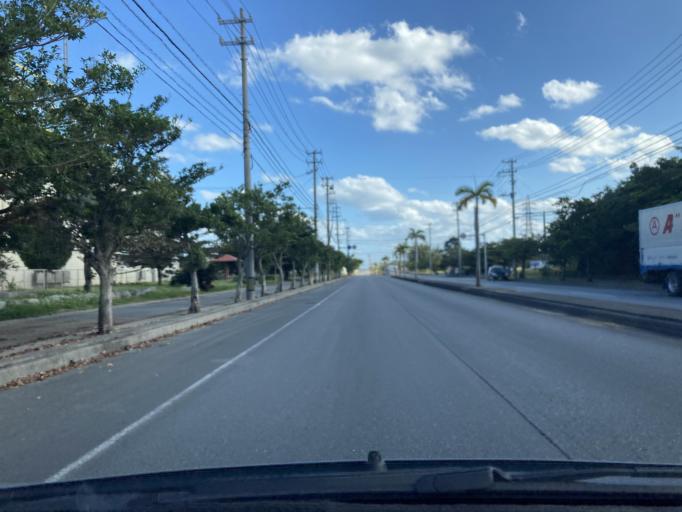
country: JP
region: Okinawa
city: Katsuren-haebaru
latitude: 26.3329
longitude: 127.8523
